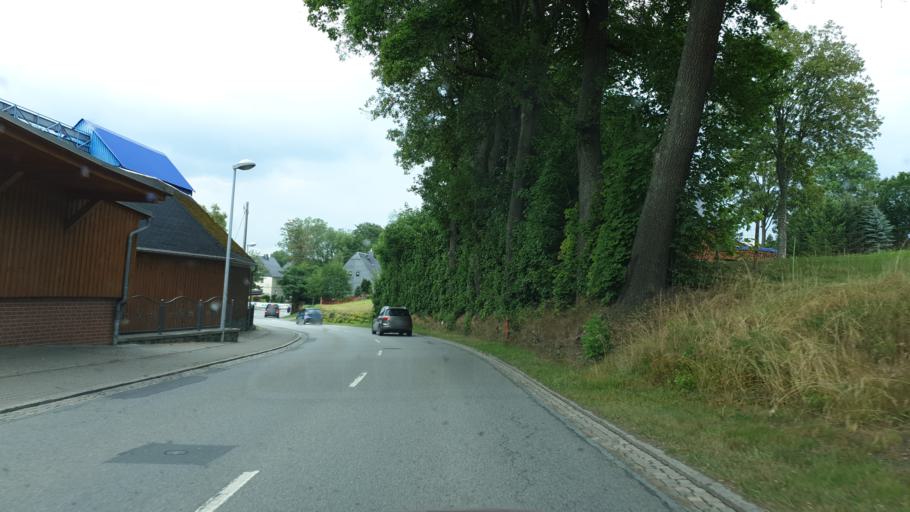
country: DE
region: Saxony
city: Zwonitz
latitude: 50.6407
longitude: 12.8192
